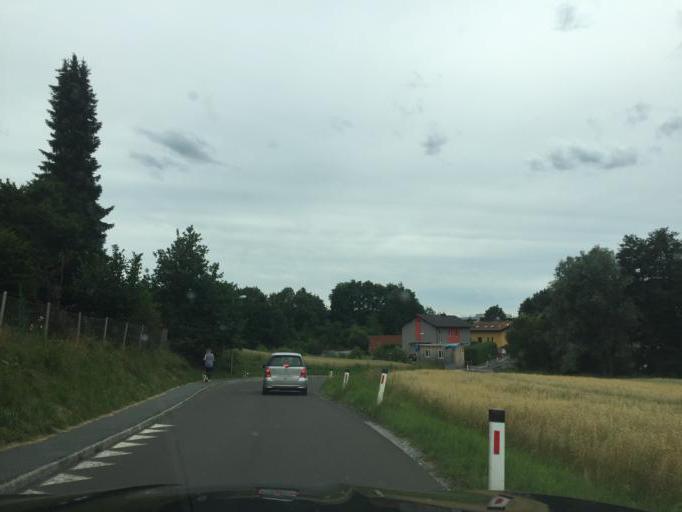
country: AT
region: Styria
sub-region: Politischer Bezirk Graz-Umgebung
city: Hart bei Graz
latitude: 47.0482
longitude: 15.5116
